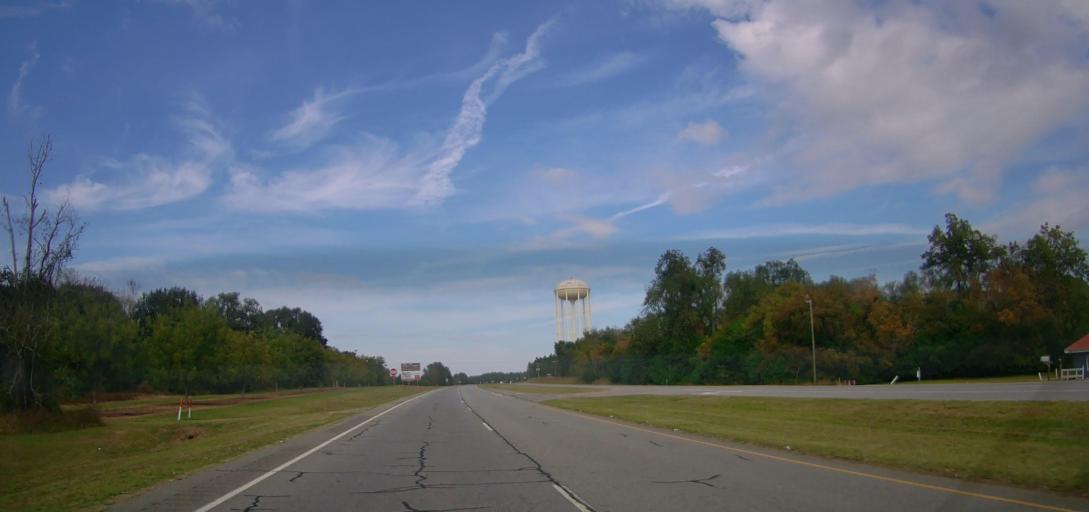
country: US
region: Georgia
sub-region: Mitchell County
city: Camilla
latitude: 31.2710
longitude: -84.1925
